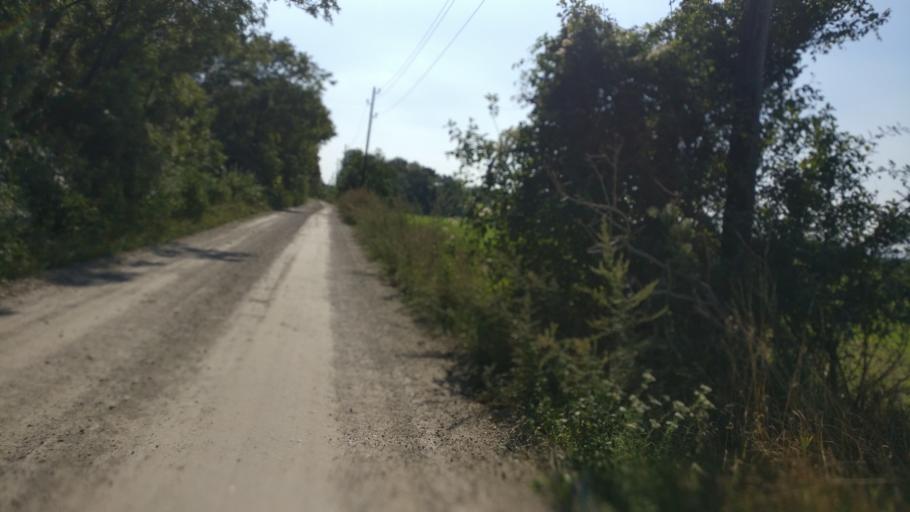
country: AT
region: Lower Austria
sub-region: Politischer Bezirk Baden
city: Ebreichsdorf
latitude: 47.9798
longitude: 16.4043
